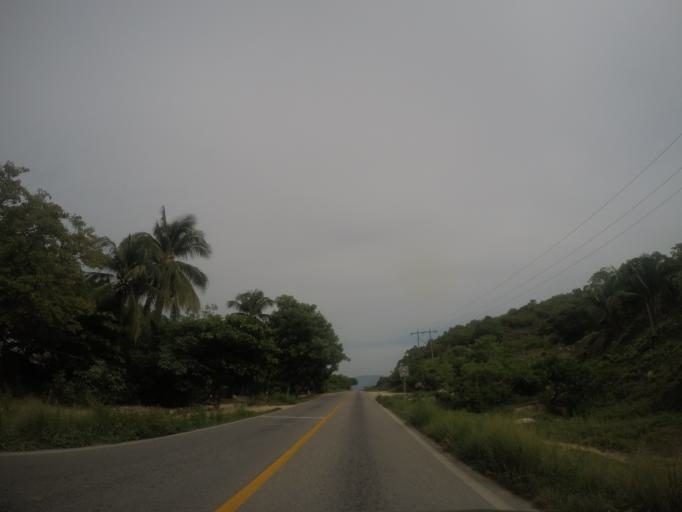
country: MX
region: Oaxaca
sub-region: Villa de Tututepec de Melchor Ocampo
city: Santa Rosa de Lima
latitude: 15.9727
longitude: -97.4001
